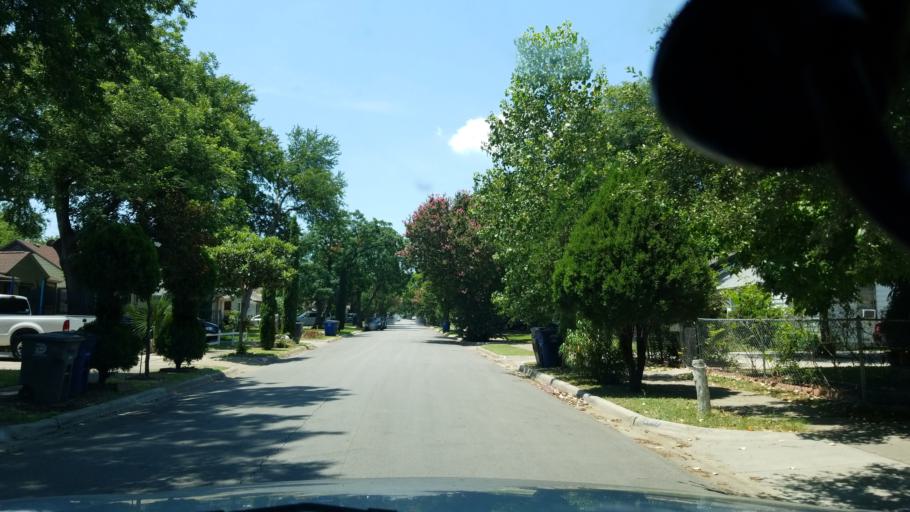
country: US
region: Texas
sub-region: Dallas County
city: Cockrell Hill
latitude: 32.7292
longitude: -96.8618
